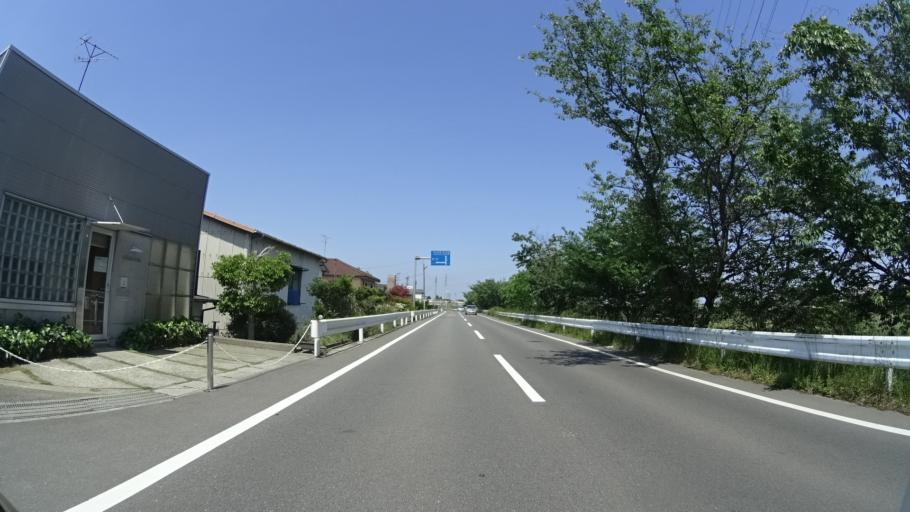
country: JP
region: Ehime
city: Hojo
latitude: 34.0450
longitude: 132.9834
